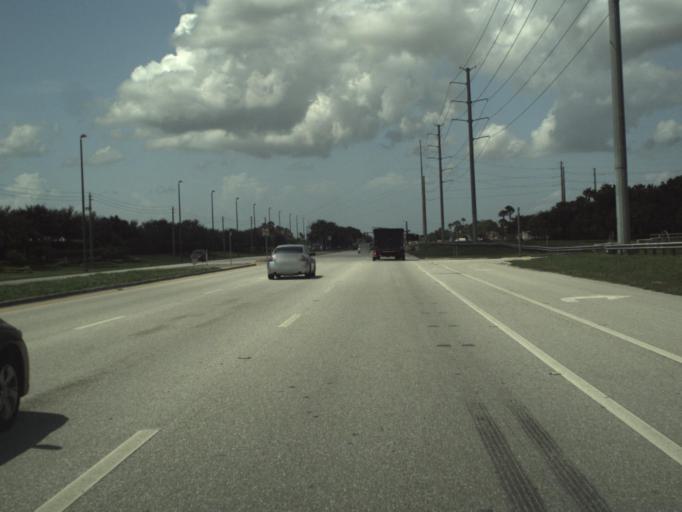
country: US
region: Florida
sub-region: Palm Beach County
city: Boca Pointe
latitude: 26.3608
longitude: -80.2033
